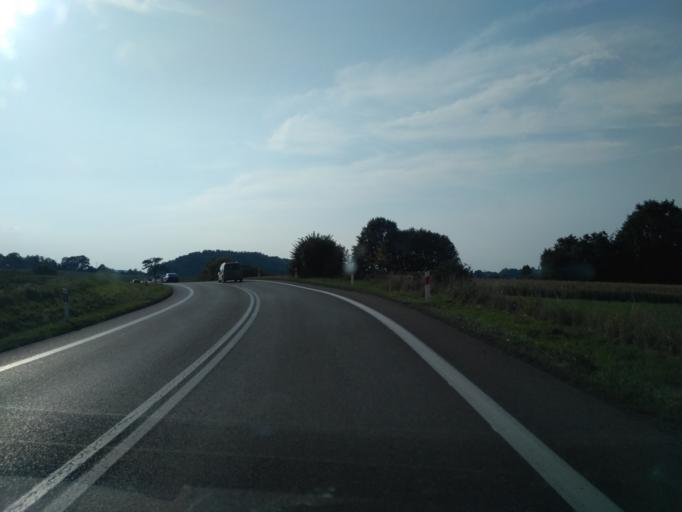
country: PL
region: Subcarpathian Voivodeship
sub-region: Powiat sanocki
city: Strachocina
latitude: 49.6079
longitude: 22.1258
